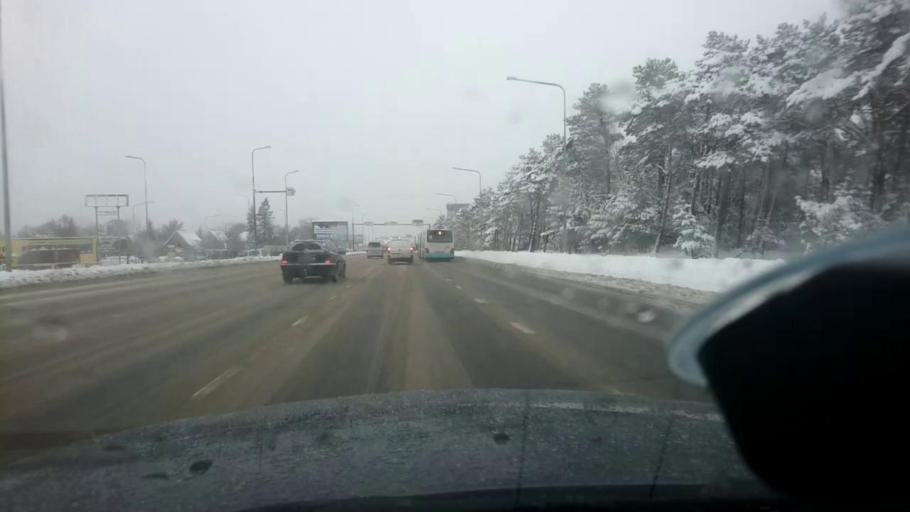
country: EE
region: Harju
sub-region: Tallinna linn
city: Tallinn
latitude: 59.3973
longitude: 24.7265
